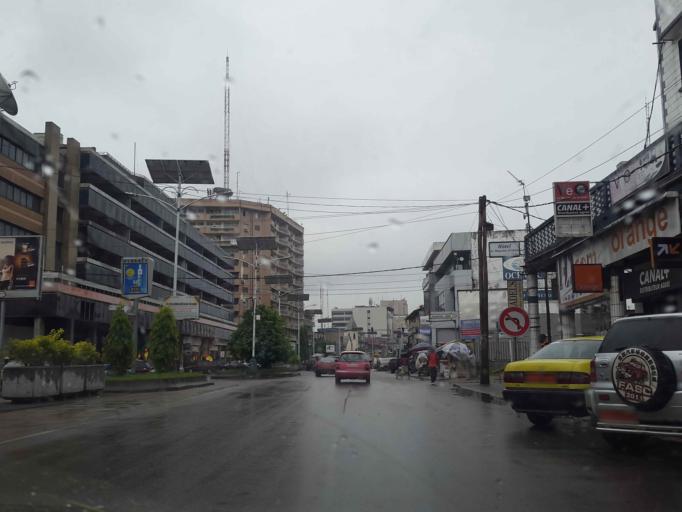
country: CM
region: Littoral
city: Douala
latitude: 4.0546
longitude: 9.6983
